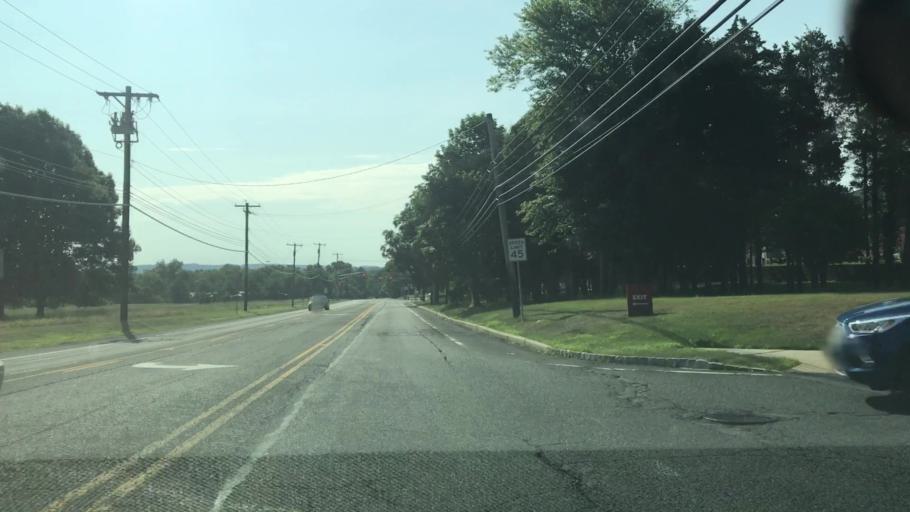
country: US
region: New Jersey
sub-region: Somerset County
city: Bridgewater
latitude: 40.6062
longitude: -74.6908
